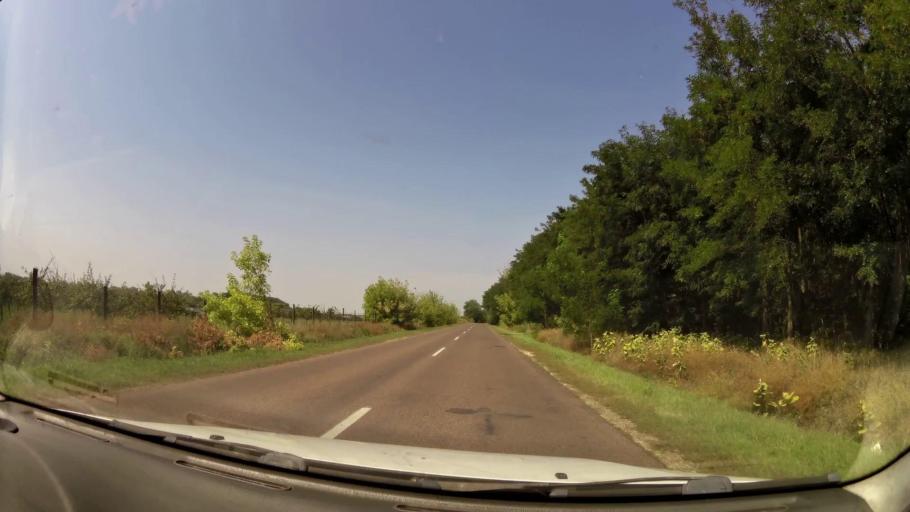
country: HU
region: Pest
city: Tapiobicske
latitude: 47.3794
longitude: 19.6636
